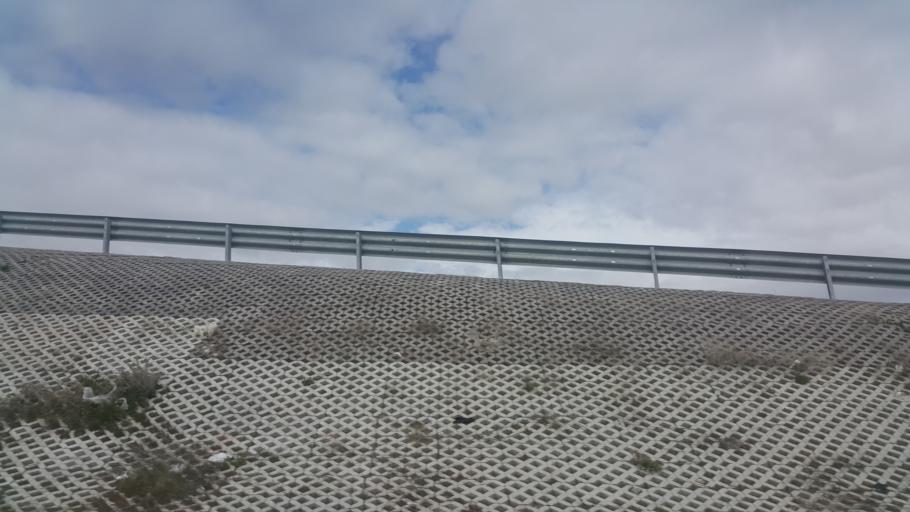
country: TR
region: Aksaray
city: Taspinar
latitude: 38.0244
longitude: 34.0467
